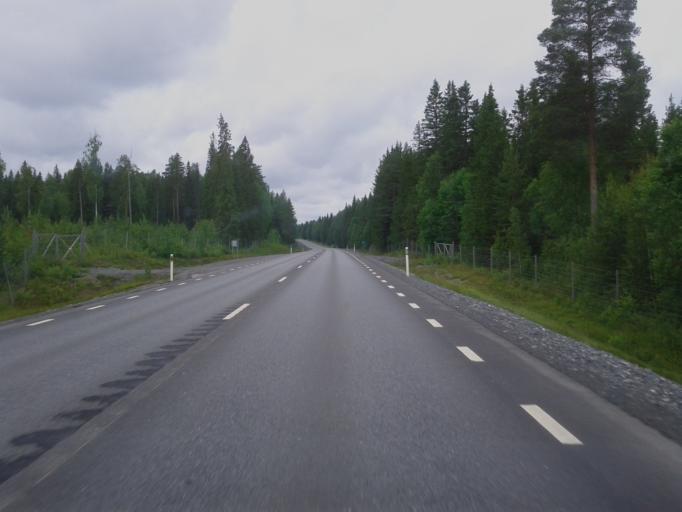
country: SE
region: Vaesterbotten
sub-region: Skelleftea Kommun
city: Forsbacka
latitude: 64.8513
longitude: 20.4867
